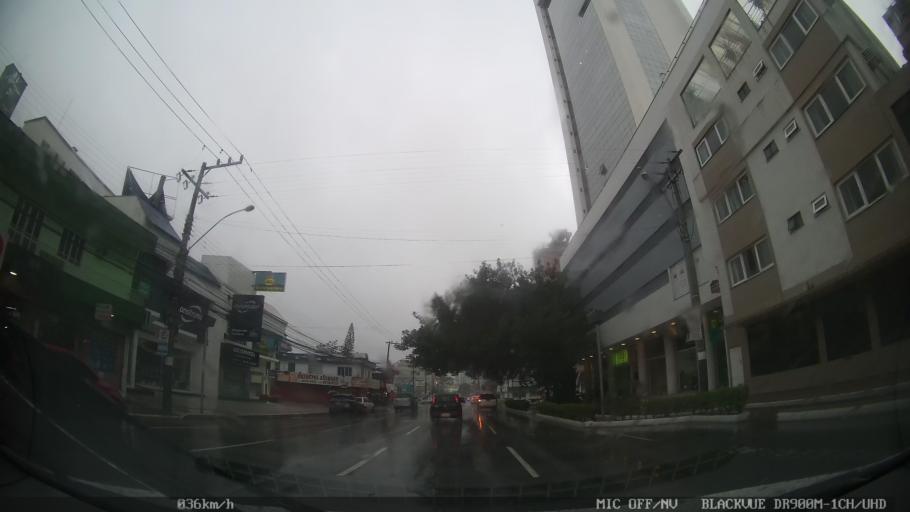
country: BR
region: Santa Catarina
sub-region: Balneario Camboriu
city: Balneario Camboriu
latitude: -26.9787
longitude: -48.6399
